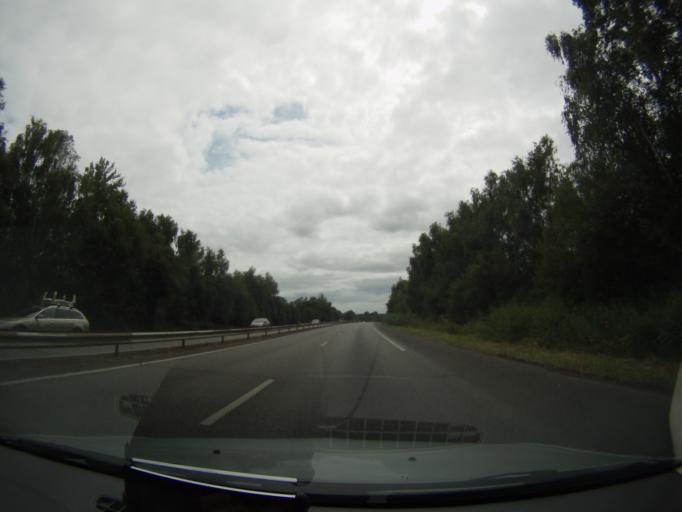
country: FR
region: Pays de la Loire
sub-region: Departement de la Loire-Atlantique
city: Orvault
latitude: 47.2881
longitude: -1.6079
